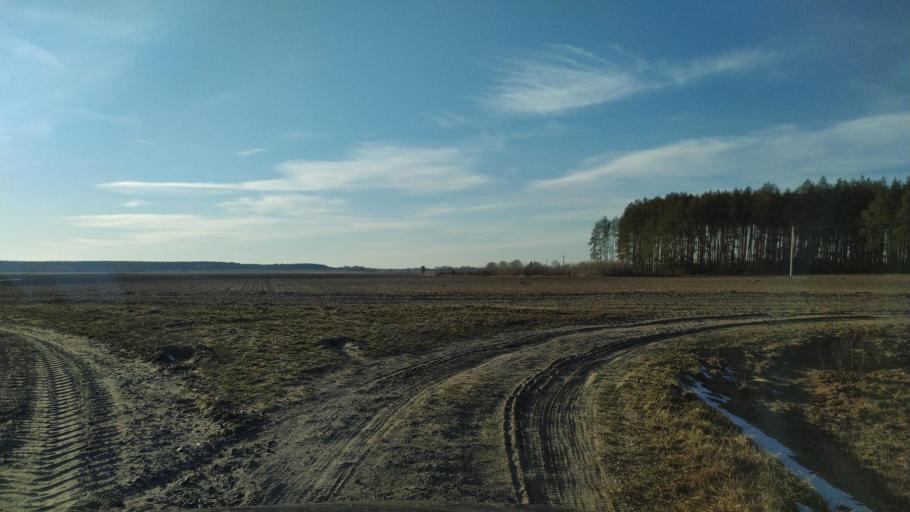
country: BY
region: Brest
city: Pruzhany
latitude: 52.5461
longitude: 24.2727
